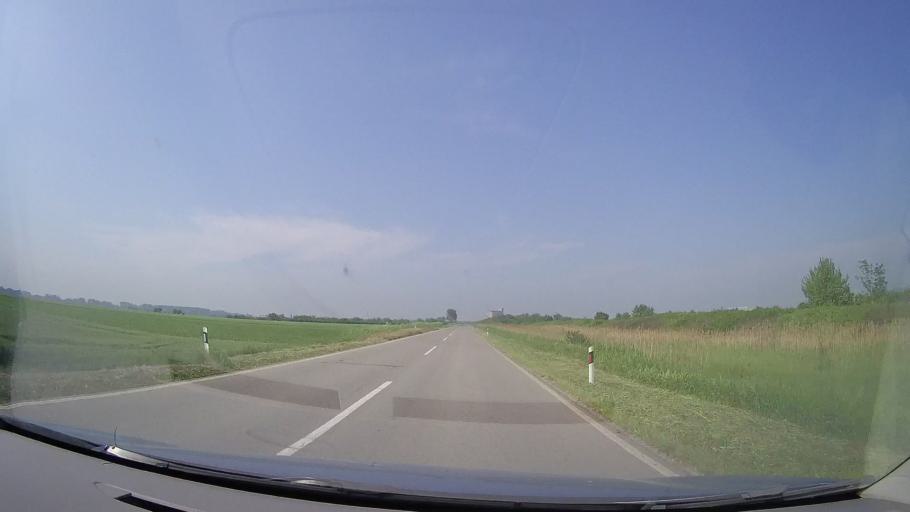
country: RS
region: Autonomna Pokrajina Vojvodina
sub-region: Srednjebanatski Okrug
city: Secanj
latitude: 45.3823
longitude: 20.7906
